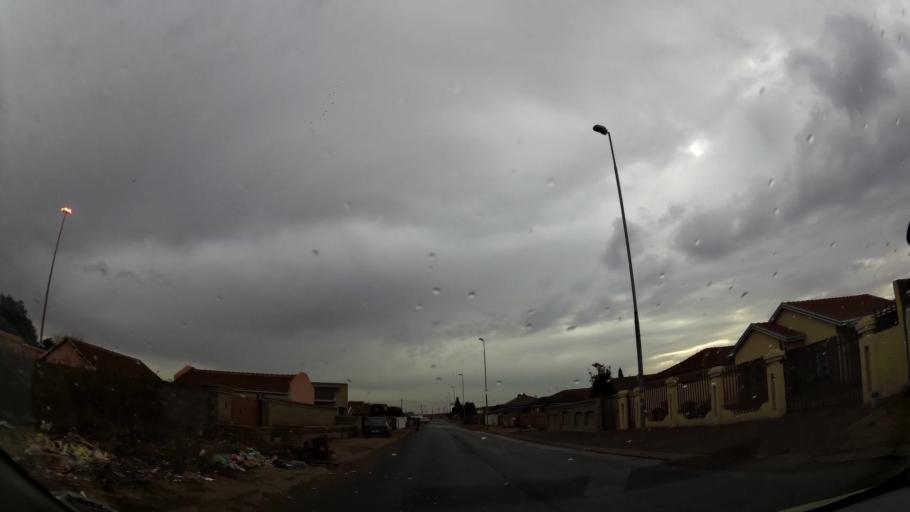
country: ZA
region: Gauteng
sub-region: Ekurhuleni Metropolitan Municipality
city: Germiston
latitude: -26.3364
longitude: 28.1979
